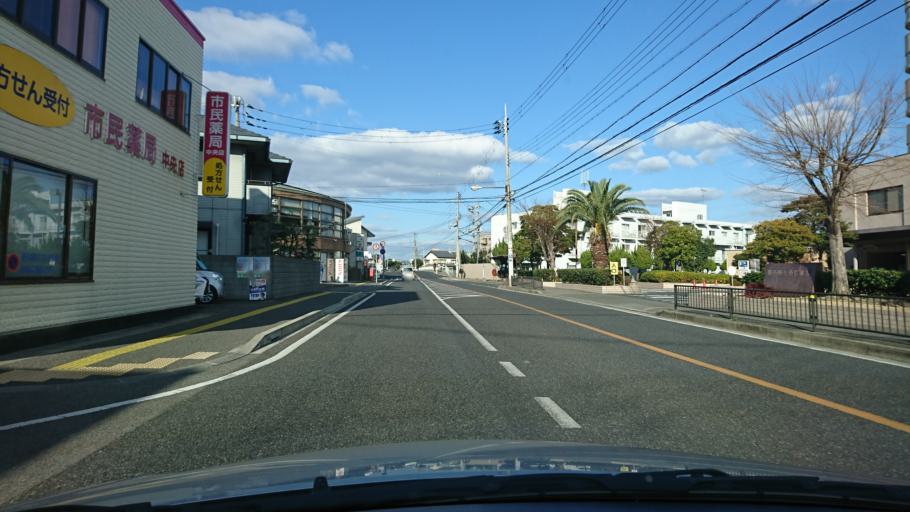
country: JP
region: Hyogo
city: Akashi
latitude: 34.6570
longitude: 134.9893
